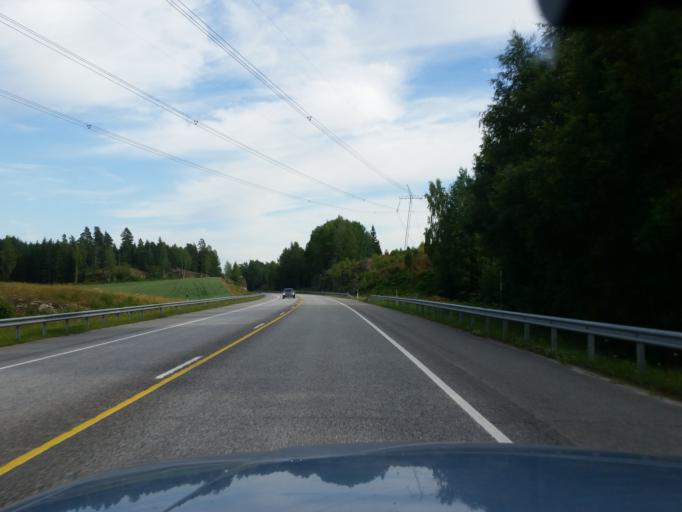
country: FI
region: Uusimaa
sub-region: Raaseporin
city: Karis
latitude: 60.0699
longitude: 23.7818
